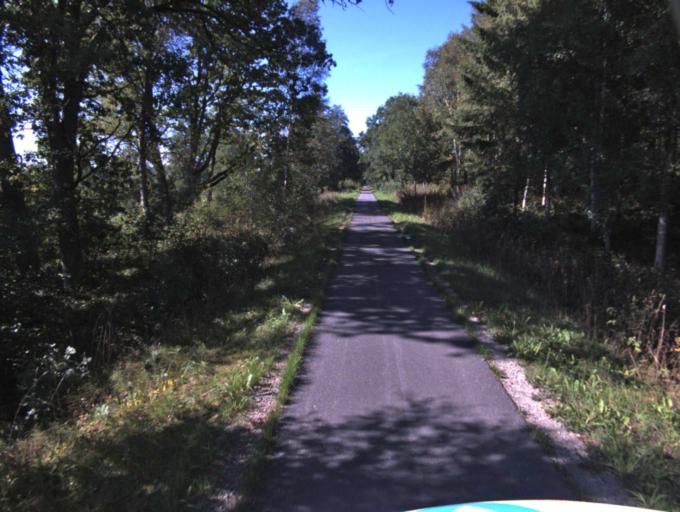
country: SE
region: Vaestra Goetaland
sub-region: Ulricehamns Kommun
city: Ulricehamn
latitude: 57.7994
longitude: 13.3863
